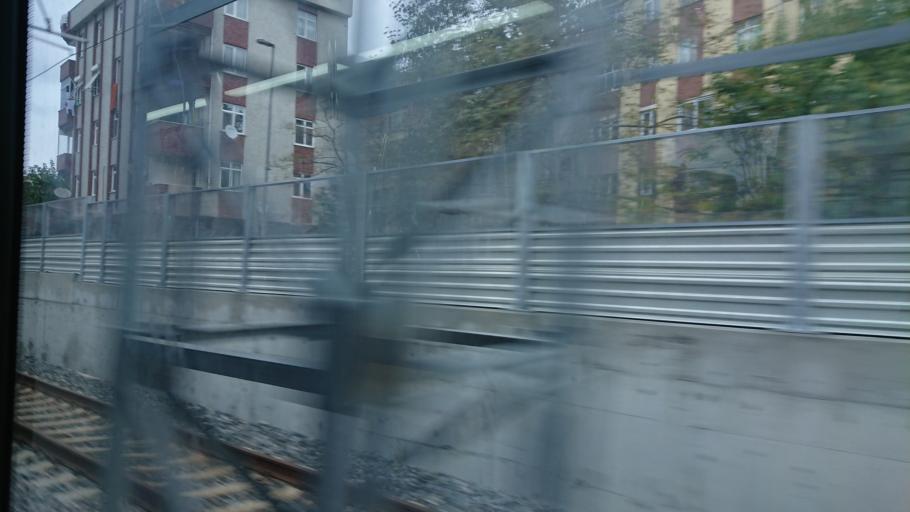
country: TR
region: Istanbul
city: Mahmutbey
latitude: 40.9952
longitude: 28.7682
